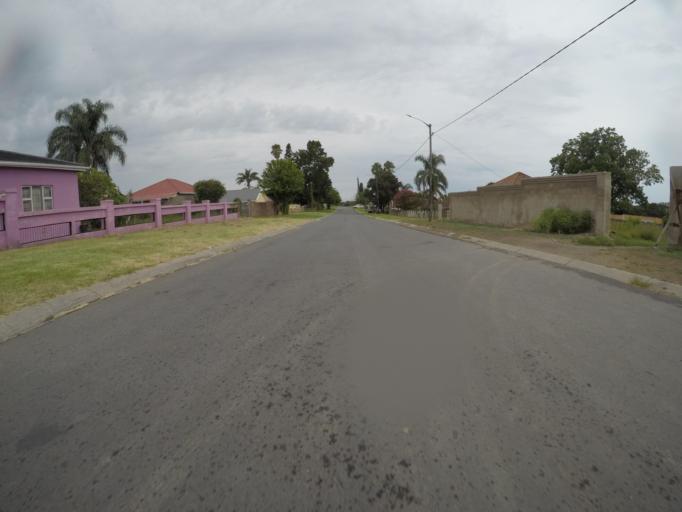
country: ZA
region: Eastern Cape
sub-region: Buffalo City Metropolitan Municipality
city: East London
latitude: -32.9670
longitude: 27.8317
